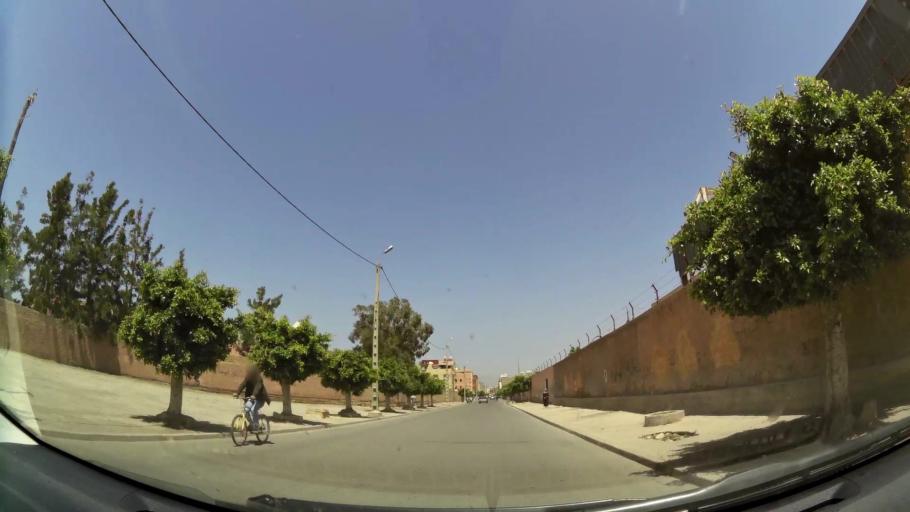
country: MA
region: Souss-Massa-Draa
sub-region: Inezgane-Ait Mellou
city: Inezgane
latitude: 30.3452
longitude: -9.4920
